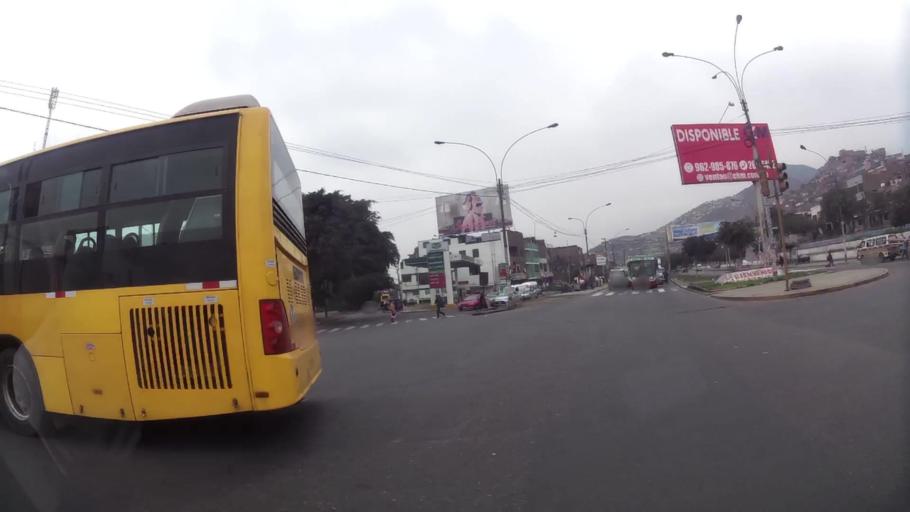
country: PE
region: Lima
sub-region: Lima
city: Independencia
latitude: -11.9765
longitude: -77.0596
